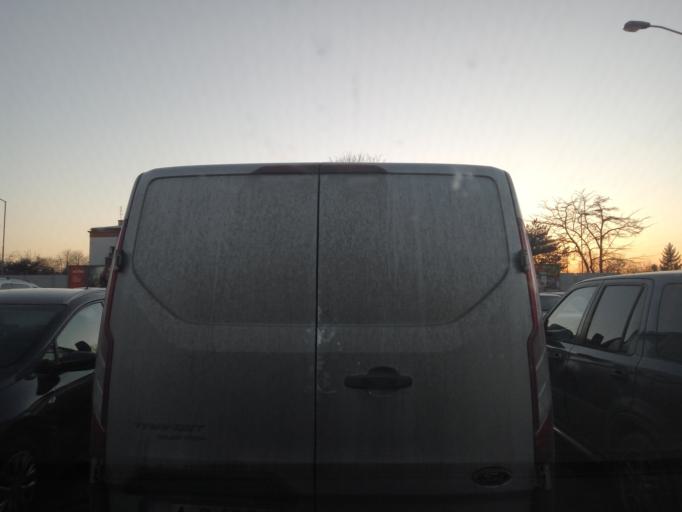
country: PL
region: Lower Silesian Voivodeship
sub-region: Powiat wroclawski
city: Wroclaw
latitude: 51.1225
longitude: 16.9888
